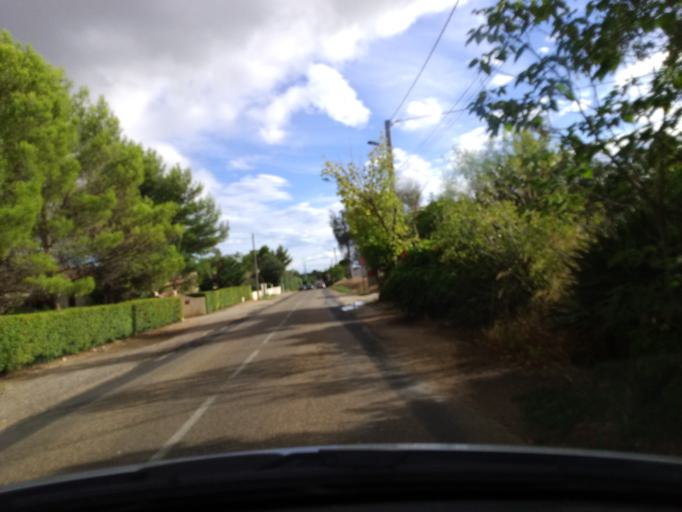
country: FR
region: Languedoc-Roussillon
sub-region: Departement de l'Herault
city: Saint-Jean-de-Fos
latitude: 43.6973
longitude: 3.5473
